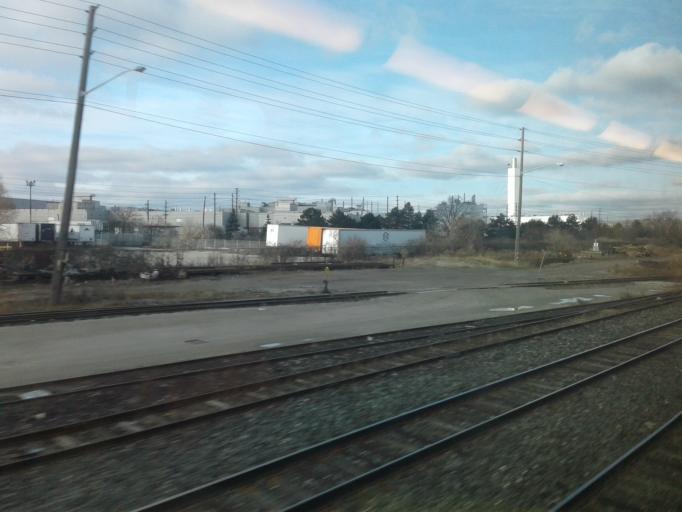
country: CA
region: Ontario
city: Oakville
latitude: 43.4785
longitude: -79.6630
